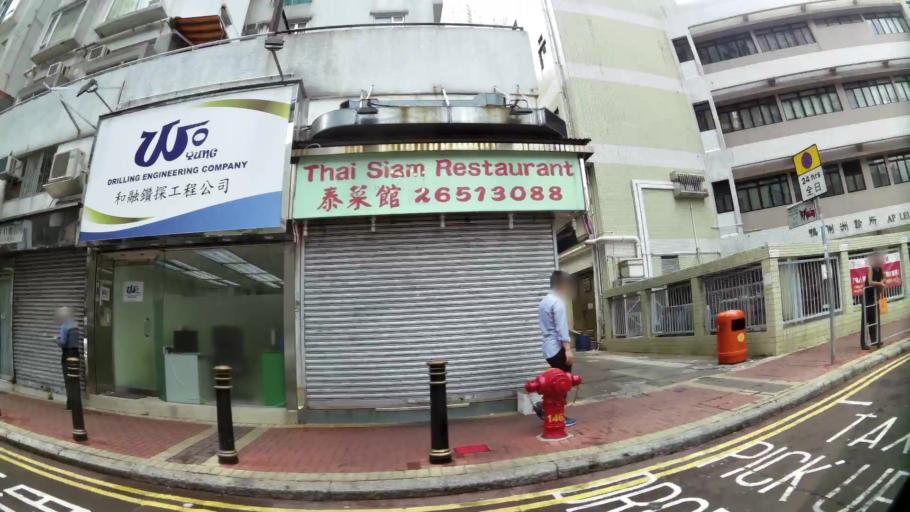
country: HK
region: Central and Western
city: Central
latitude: 22.2434
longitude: 114.1538
